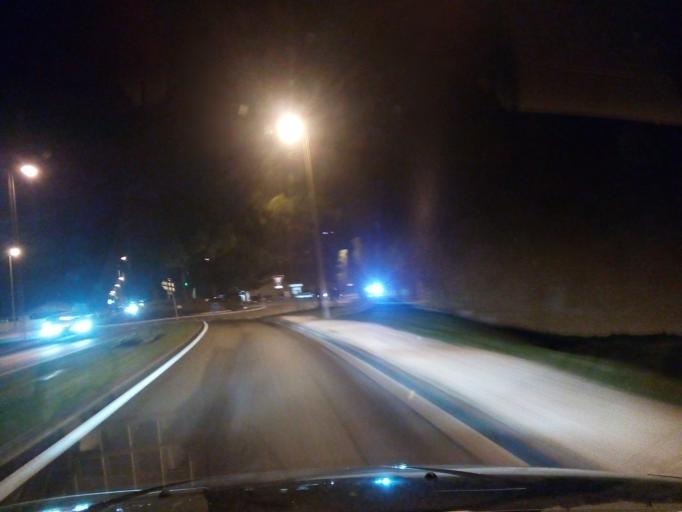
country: FR
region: Aquitaine
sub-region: Departement de la Gironde
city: Martignas-sur-Jalle
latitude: 44.8098
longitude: -0.7761
